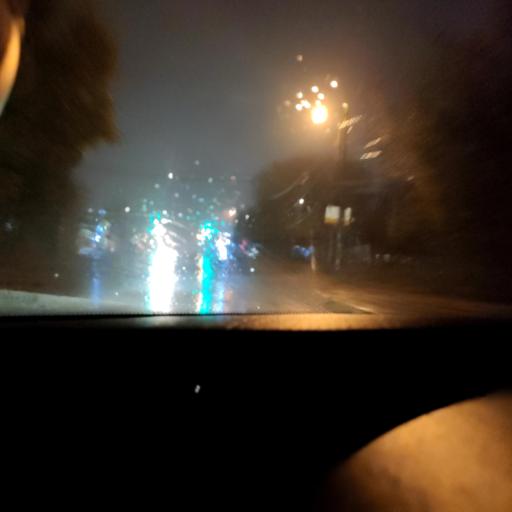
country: RU
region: Samara
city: Samara
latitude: 53.1821
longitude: 50.1643
